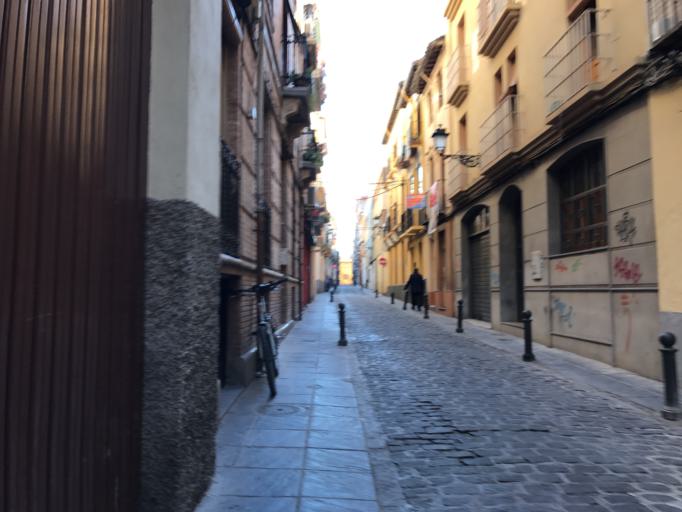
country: ES
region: Andalusia
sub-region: Provincia de Granada
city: Granada
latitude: 37.1777
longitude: -3.6045
